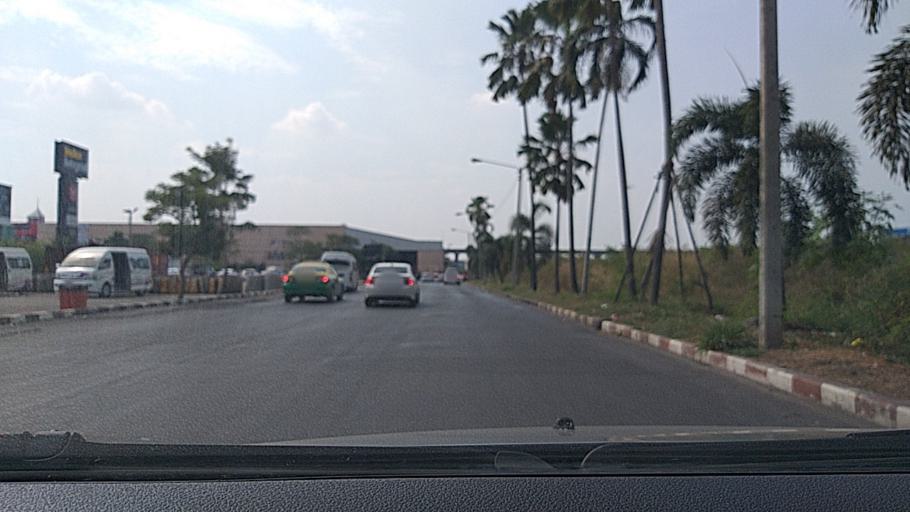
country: TH
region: Phra Nakhon Si Ayutthaya
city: Ban Bang Kadi Pathum Thani
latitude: 13.9932
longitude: 100.6190
